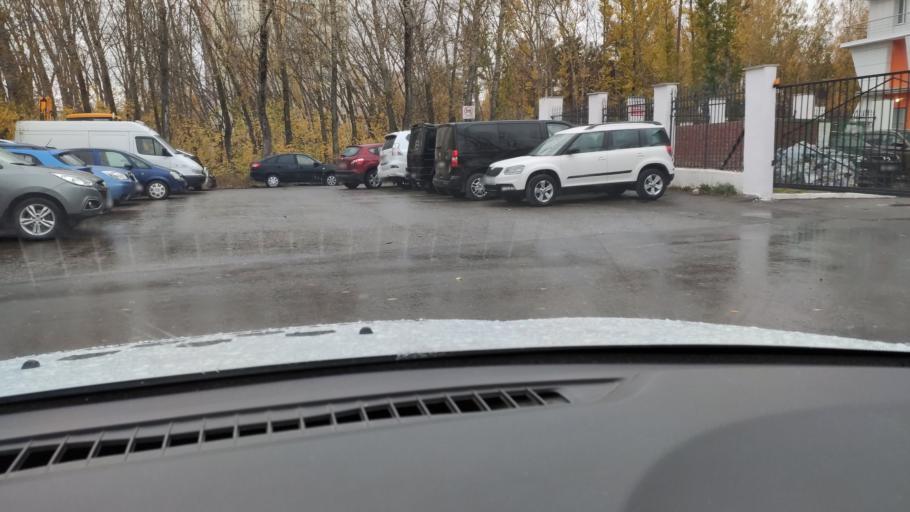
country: RU
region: Perm
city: Perm
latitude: 57.9968
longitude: 56.1899
